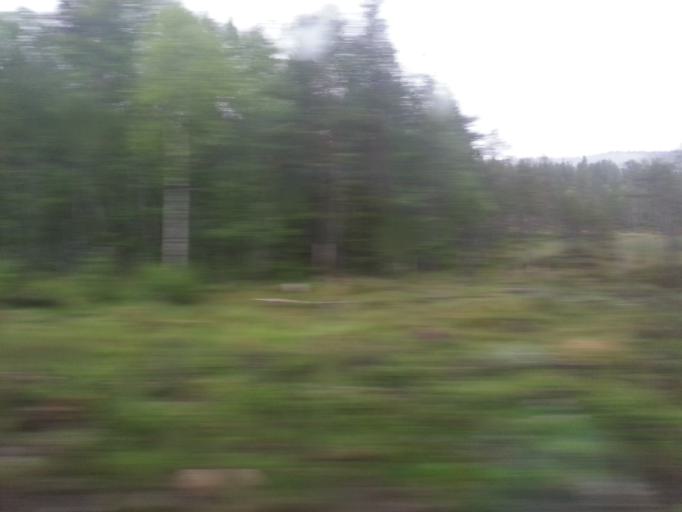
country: NO
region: Sor-Trondelag
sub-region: Rennebu
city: Berkak
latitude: 62.6814
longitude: 9.9371
